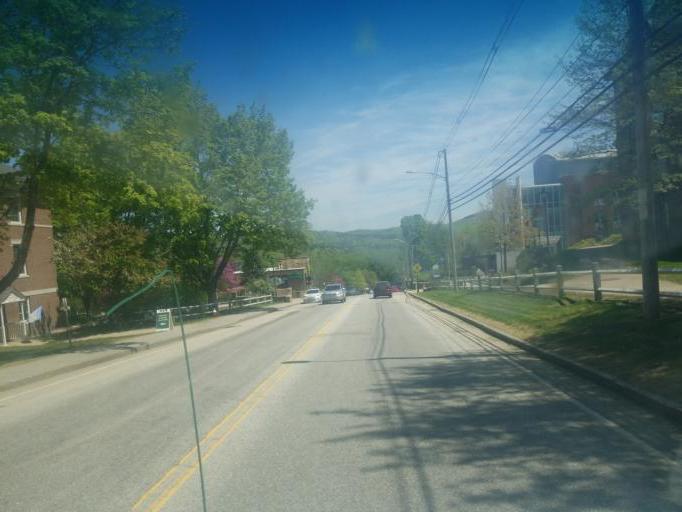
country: US
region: New Hampshire
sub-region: Grafton County
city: Plymouth
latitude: 43.7579
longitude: -71.6909
